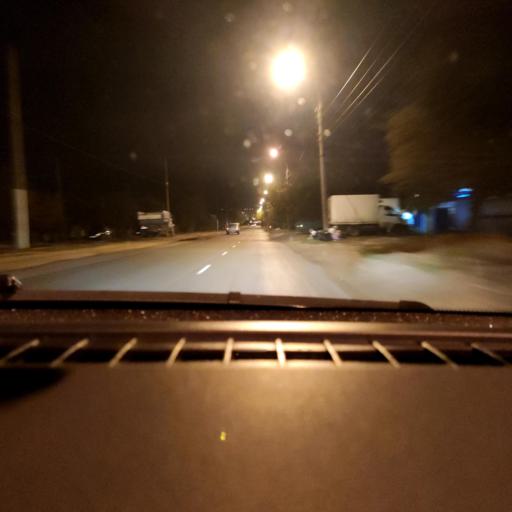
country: RU
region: Voronezj
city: Voronezh
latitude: 51.6977
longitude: 39.1723
